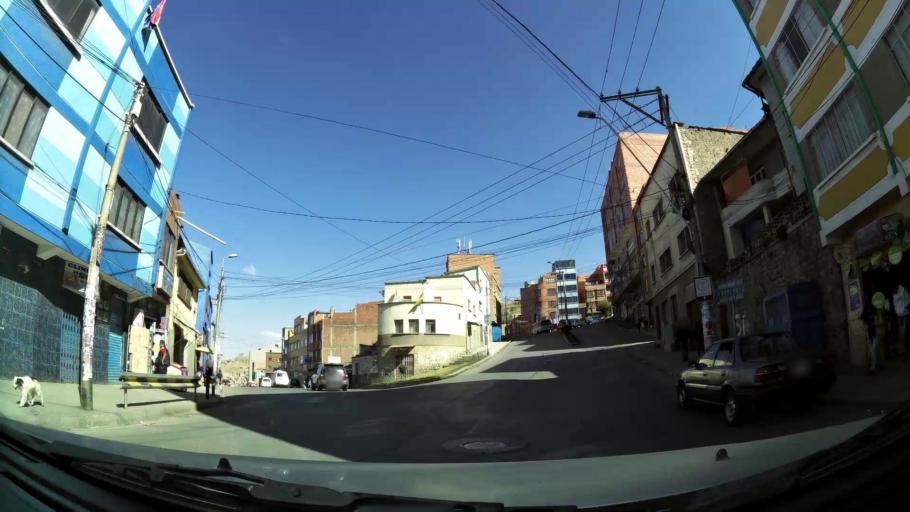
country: BO
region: La Paz
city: La Paz
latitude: -16.5097
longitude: -68.1436
